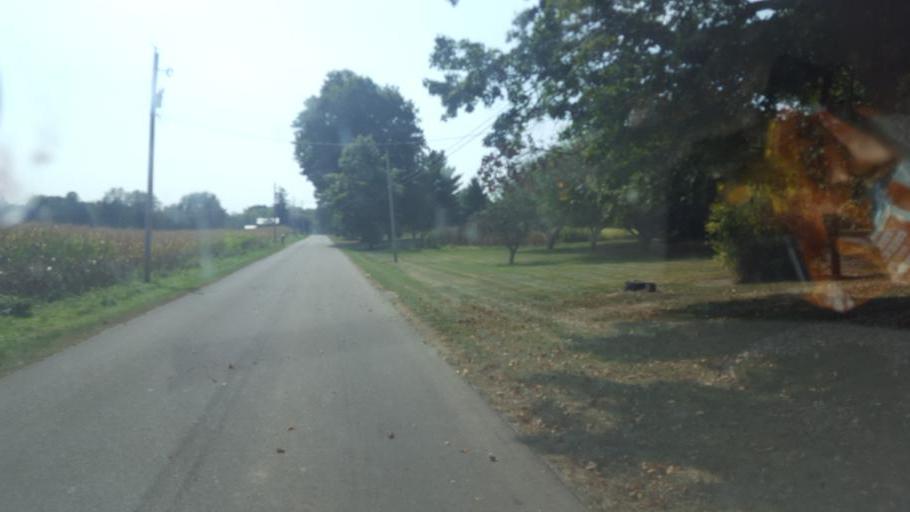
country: US
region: Ohio
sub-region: Morrow County
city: Mount Gilead
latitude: 40.5700
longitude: -82.8436
